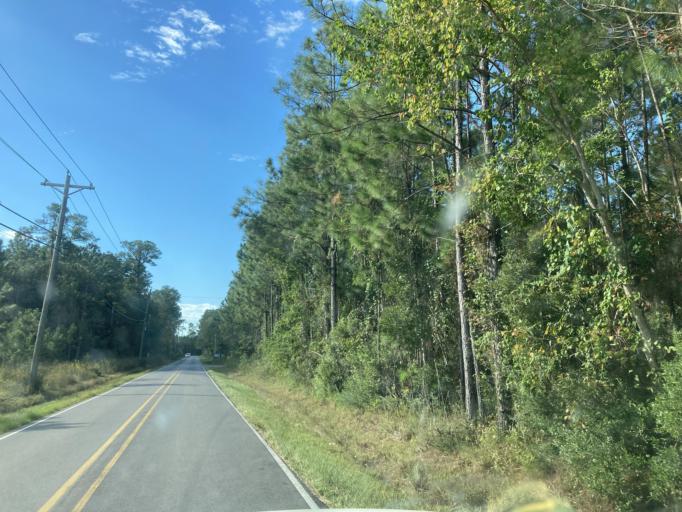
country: US
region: Mississippi
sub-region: Jackson County
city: Saint Martin
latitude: 30.4393
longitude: -88.8665
